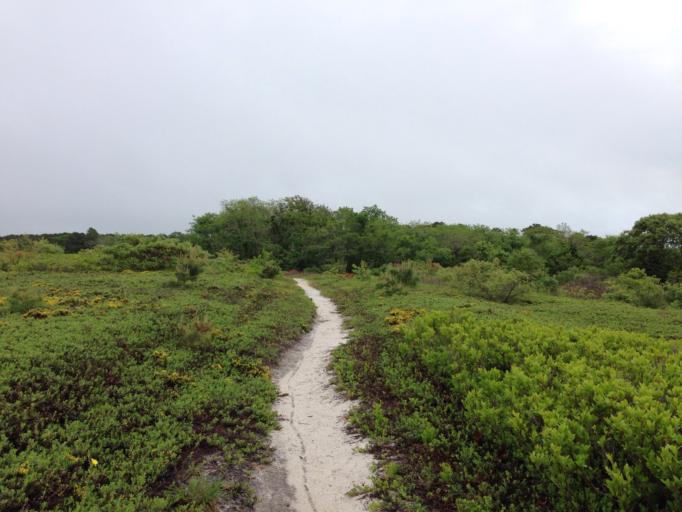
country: US
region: Massachusetts
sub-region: Barnstable County
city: North Eastham
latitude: 41.8851
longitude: -69.9957
